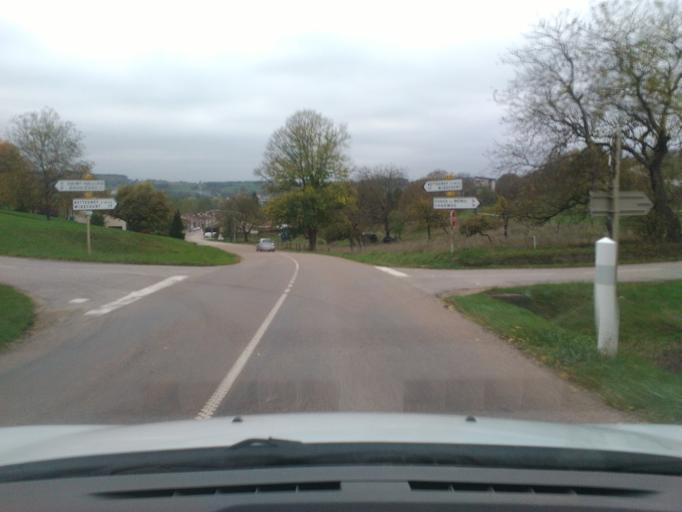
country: FR
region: Lorraine
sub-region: Departement des Vosges
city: Vincey
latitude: 48.3017
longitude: 6.3119
